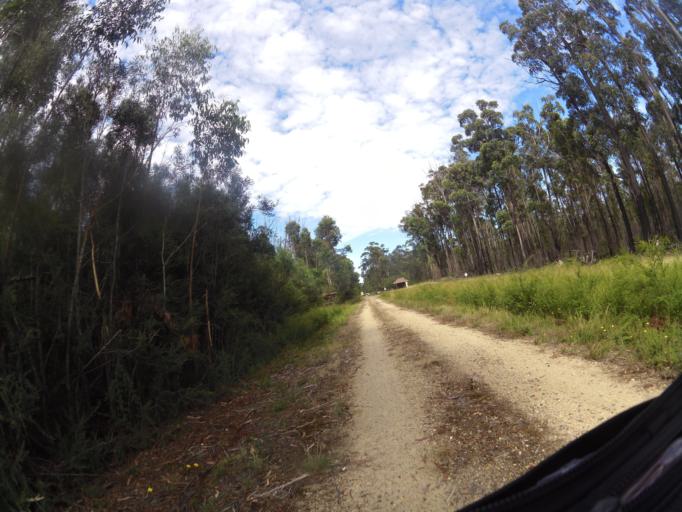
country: AU
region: Victoria
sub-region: East Gippsland
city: Lakes Entrance
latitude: -37.7477
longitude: 148.2264
